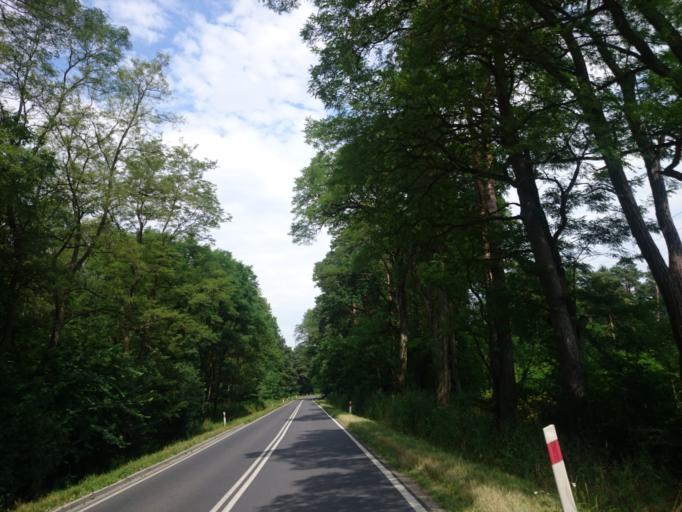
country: PL
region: West Pomeranian Voivodeship
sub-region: Powiat gryfinski
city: Chojna
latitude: 52.9351
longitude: 14.3821
